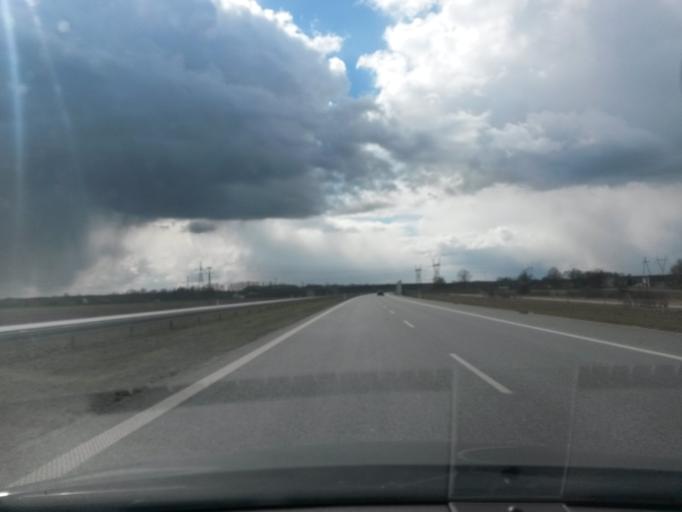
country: PL
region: Greater Poland Voivodeship
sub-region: Powiat koninski
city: Krzymow
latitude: 52.1444
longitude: 18.4134
